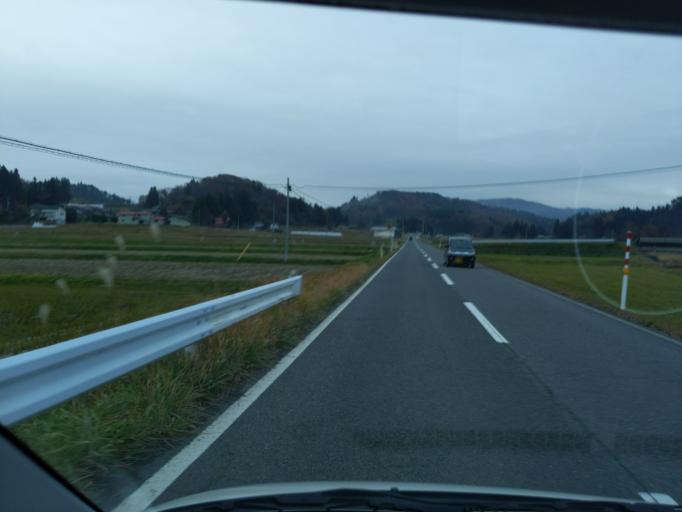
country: JP
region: Iwate
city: Kitakami
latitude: 39.2289
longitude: 141.2555
